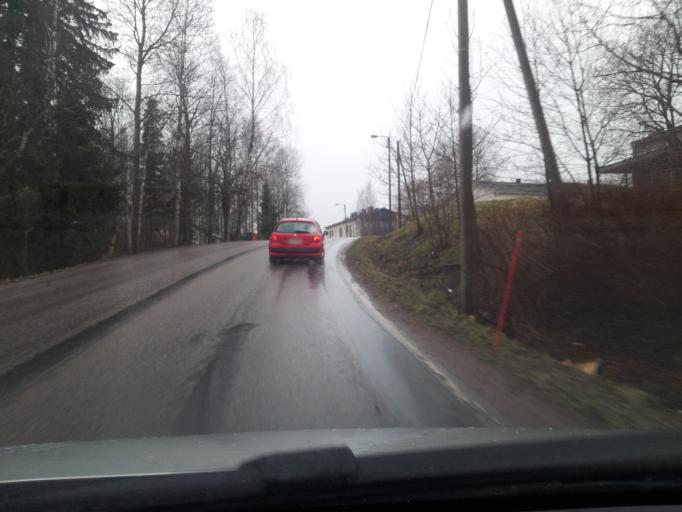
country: FI
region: Uusimaa
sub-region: Helsinki
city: Kirkkonummi
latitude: 60.1578
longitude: 24.5342
